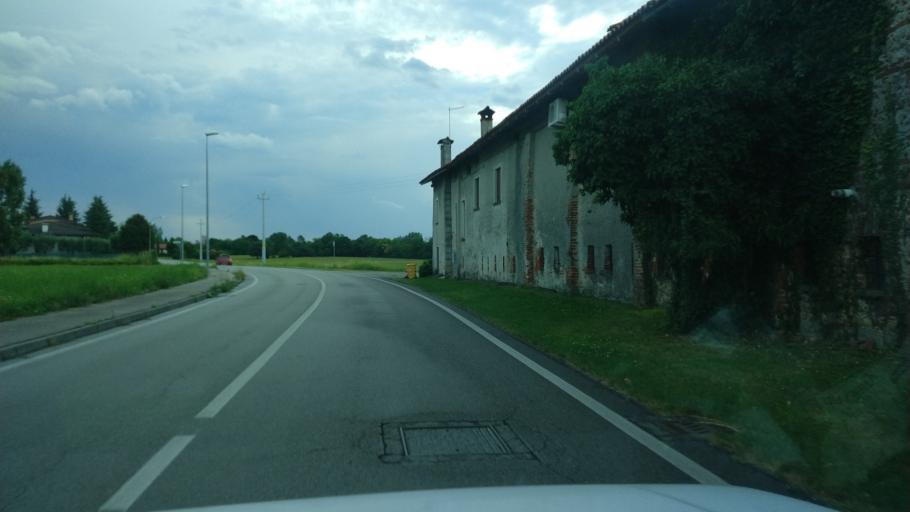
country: IT
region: Veneto
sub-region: Provincia di Vicenza
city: Bassano del Grappa
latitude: 45.7551
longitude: 11.7055
